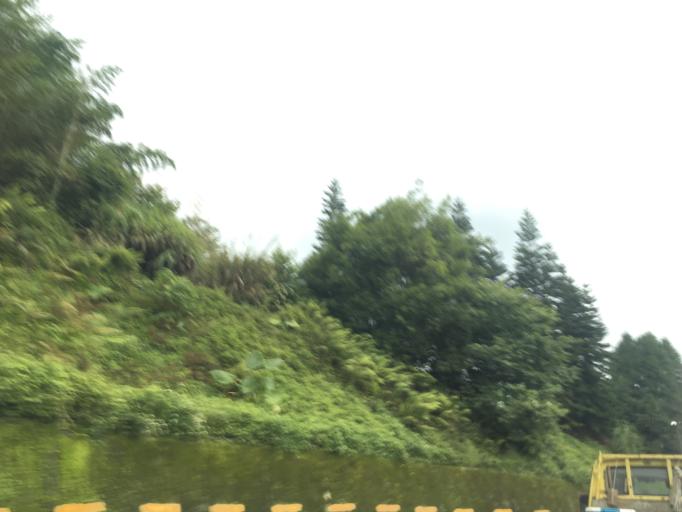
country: TW
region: Taiwan
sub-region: Chiayi
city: Jiayi Shi
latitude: 23.4605
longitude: 120.6855
